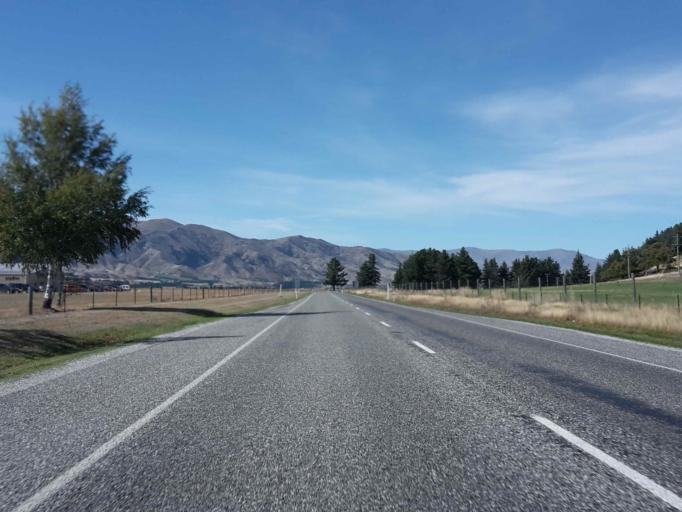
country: NZ
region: Otago
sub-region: Queenstown-Lakes District
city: Wanaka
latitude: -44.7251
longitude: 169.2446
